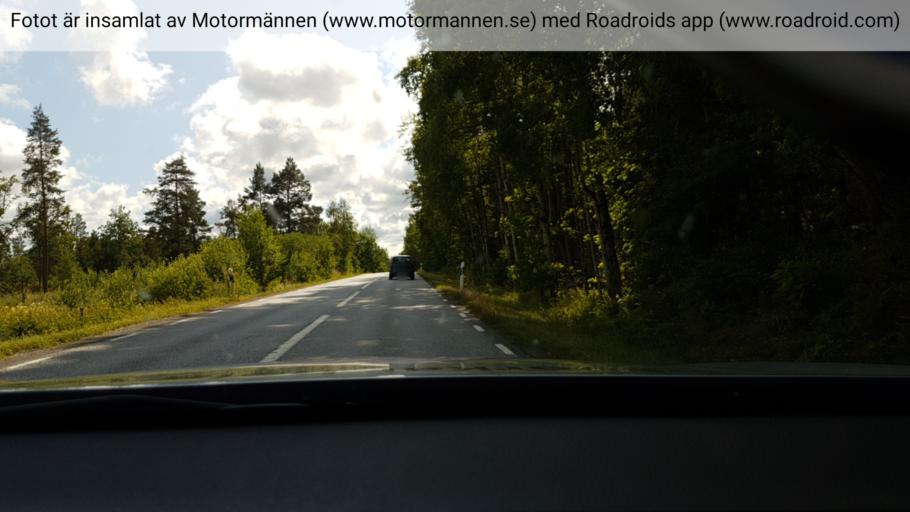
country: SE
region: Stockholm
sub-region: Norrtalje Kommun
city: Norrtalje
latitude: 59.9196
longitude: 18.7090
